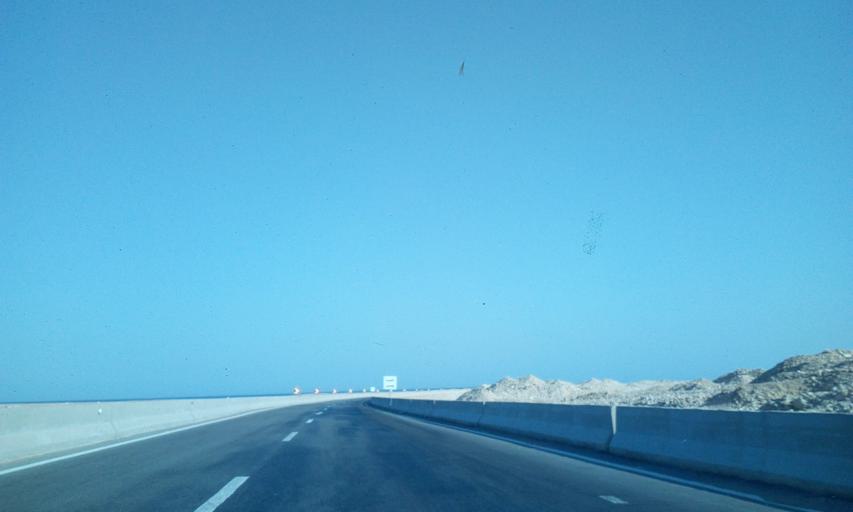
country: EG
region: As Suways
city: Ain Sukhna
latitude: 29.0951
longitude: 32.6309
